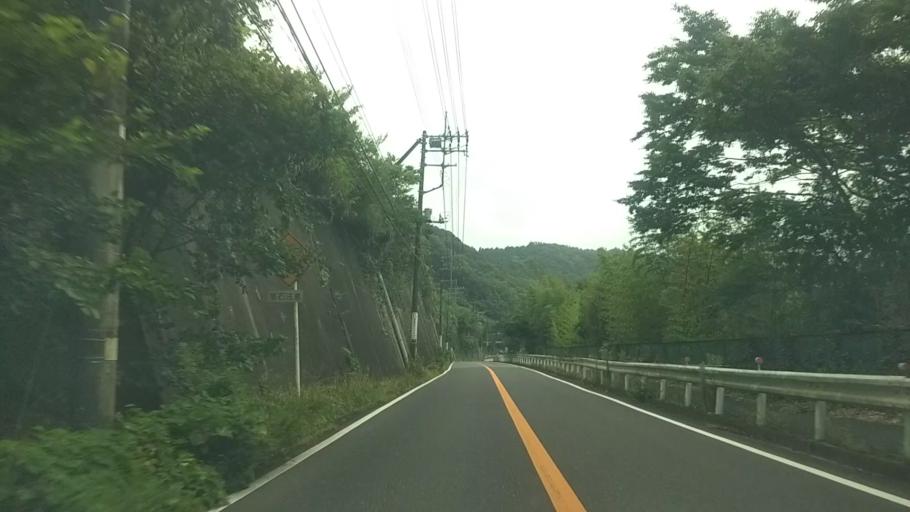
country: JP
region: Chiba
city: Kisarazu
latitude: 35.2927
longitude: 140.0811
